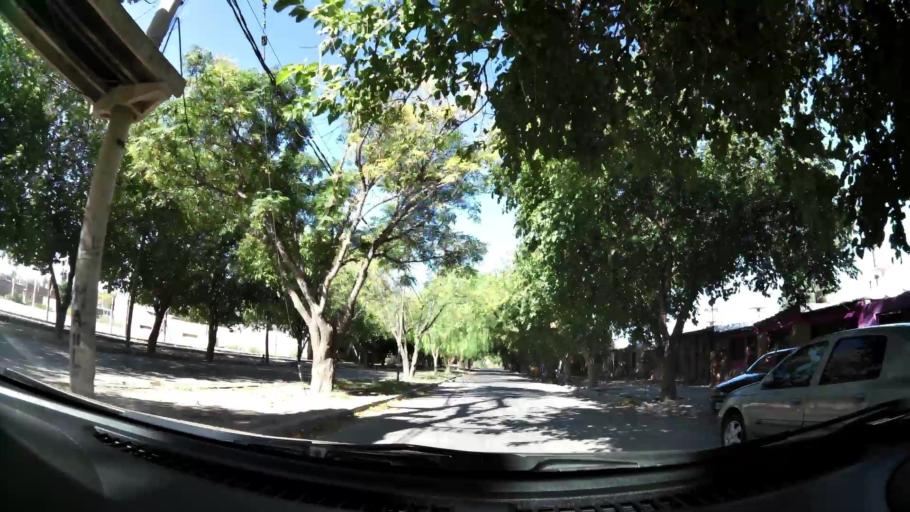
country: AR
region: Mendoza
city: Las Heras
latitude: -32.8316
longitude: -68.8306
